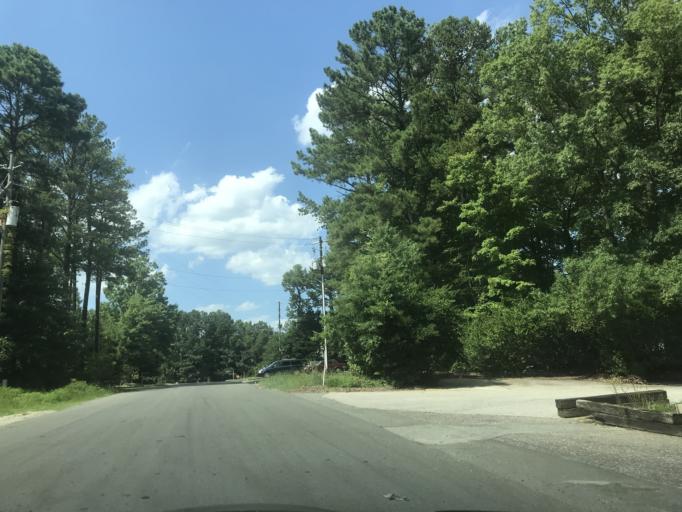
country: US
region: North Carolina
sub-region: Wake County
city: Morrisville
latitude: 35.8912
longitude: -78.7444
